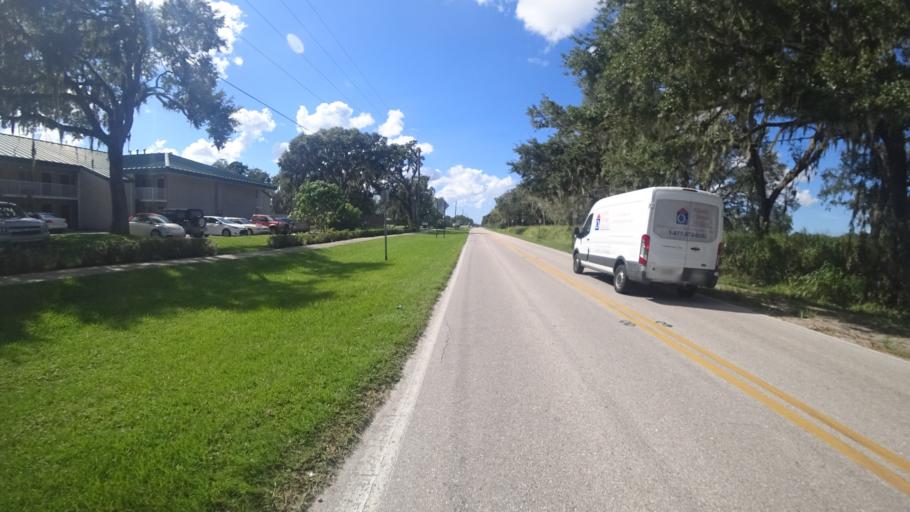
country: US
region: Florida
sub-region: Manatee County
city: Ellenton
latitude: 27.5288
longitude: -82.5139
